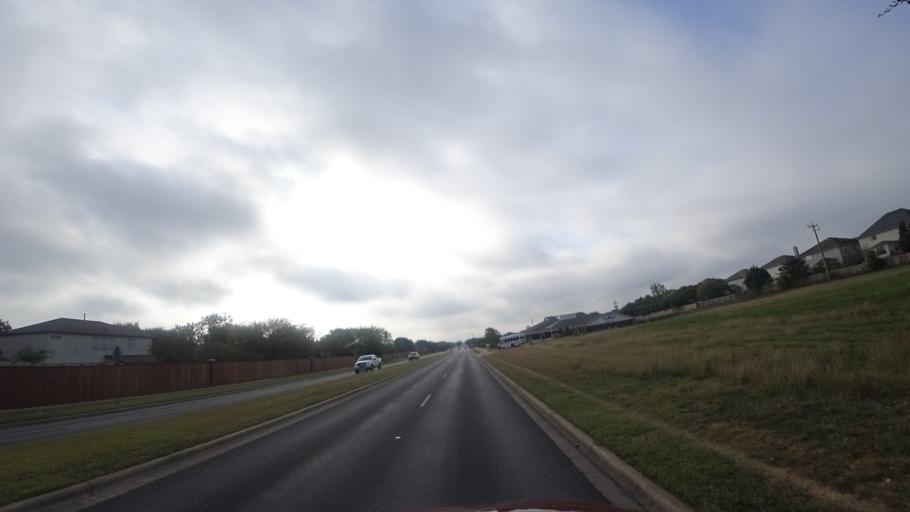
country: US
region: Texas
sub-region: Williamson County
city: Cedar Park
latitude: 30.5201
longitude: -97.8535
